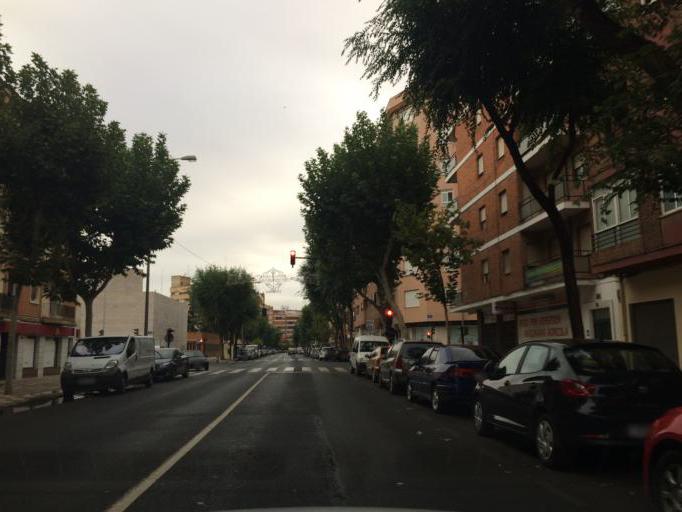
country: ES
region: Castille-La Mancha
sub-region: Provincia de Albacete
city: Albacete
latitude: 38.9985
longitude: -1.8651
